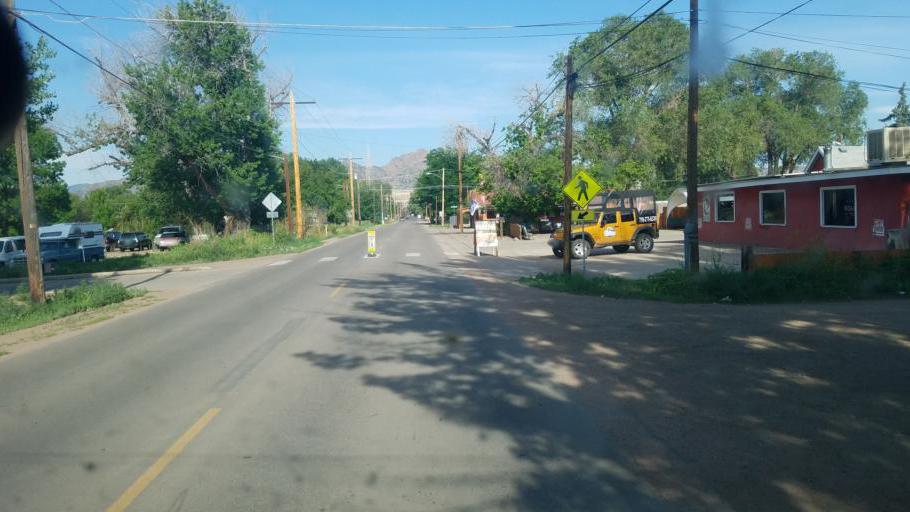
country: US
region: Colorado
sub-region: Fremont County
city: Lincoln Park
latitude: 38.4467
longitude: -105.2131
